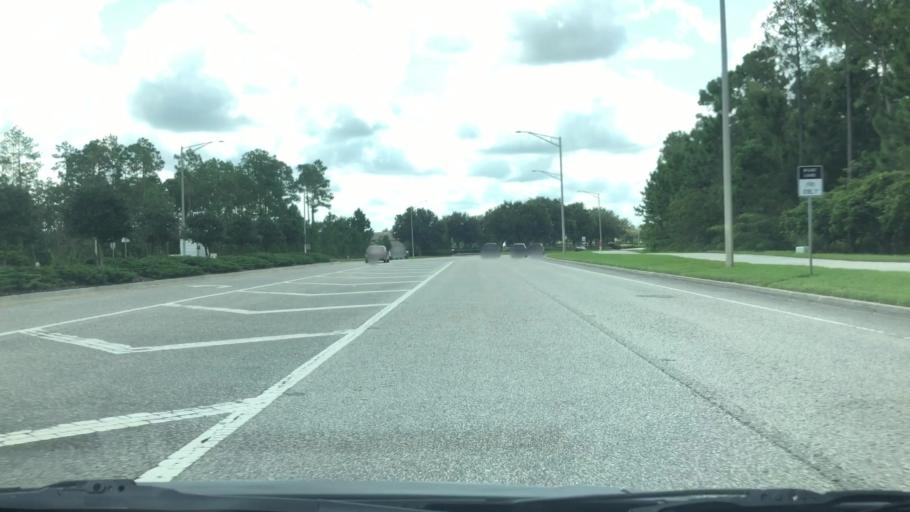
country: US
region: Florida
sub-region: Saint Johns County
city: Fruit Cove
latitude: 30.1355
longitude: -81.5454
